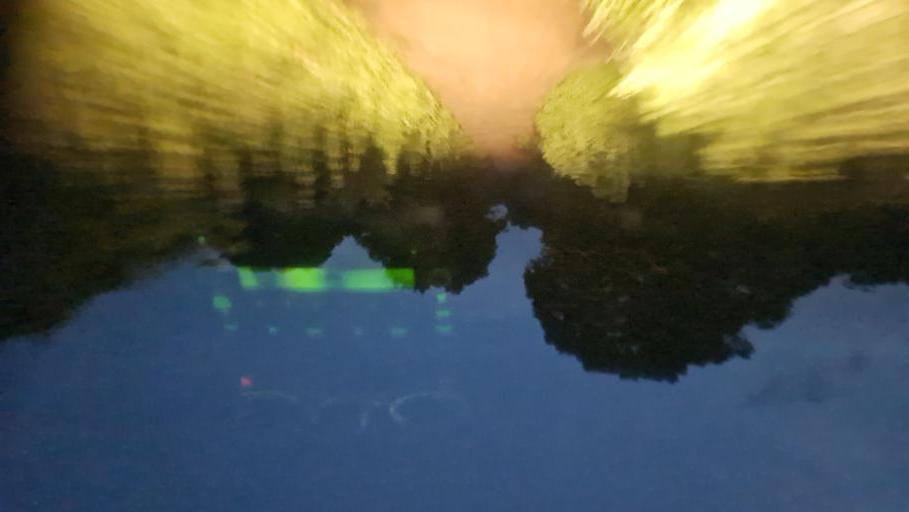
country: MZ
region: Nampula
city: Nampula
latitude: -14.6722
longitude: 39.8336
